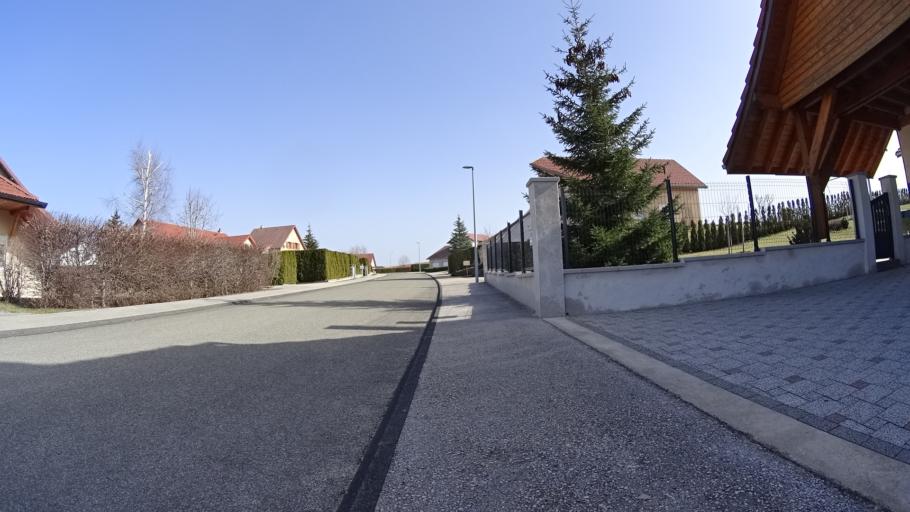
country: FR
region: Franche-Comte
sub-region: Departement du Doubs
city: Frasne
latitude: 46.8509
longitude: 6.1473
